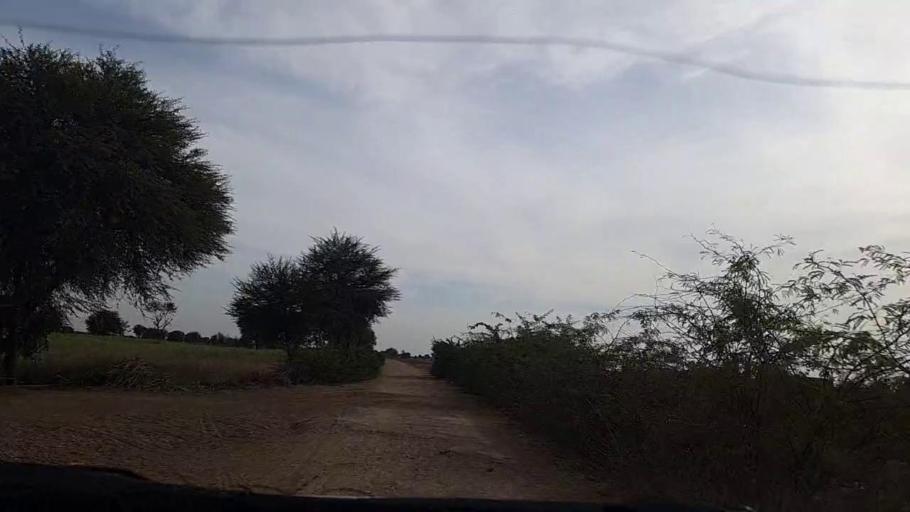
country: PK
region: Sindh
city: Dhoro Naro
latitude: 25.4114
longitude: 69.5183
